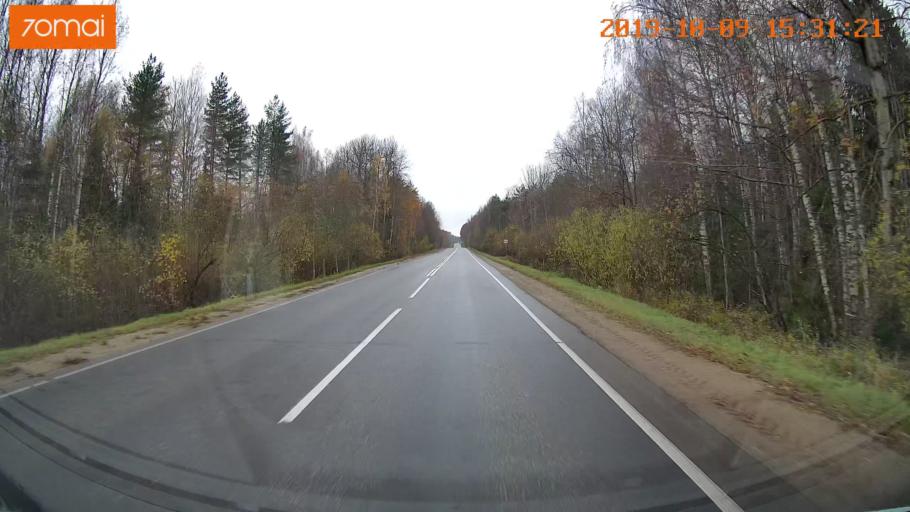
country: RU
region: Kostroma
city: Susanino
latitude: 57.9722
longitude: 41.3046
